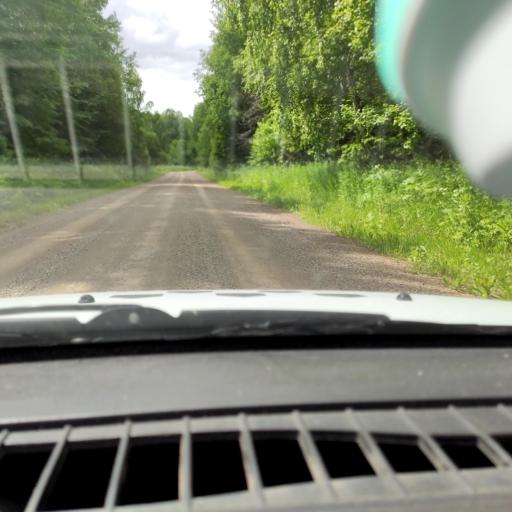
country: RU
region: Perm
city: Suksun
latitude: 57.2096
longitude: 57.6560
